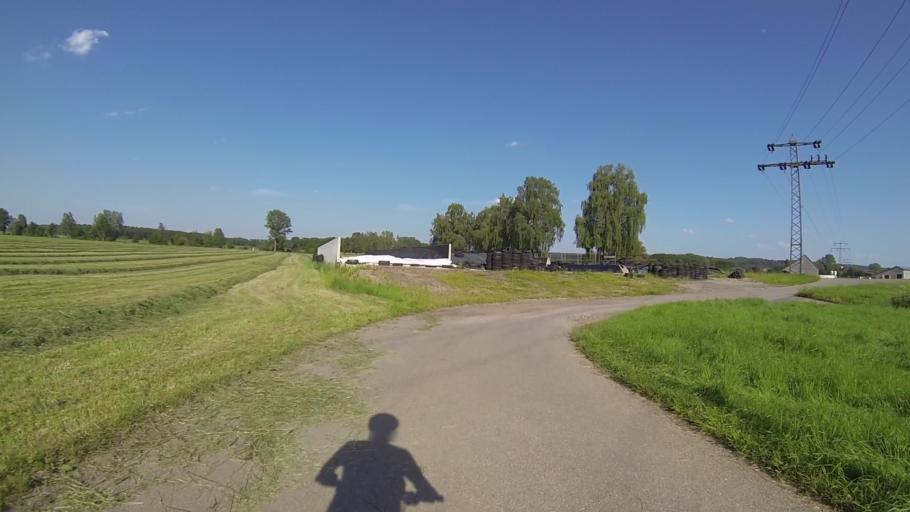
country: DE
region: Baden-Wuerttemberg
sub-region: Tuebingen Region
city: Warthausen
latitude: 48.1516
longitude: 9.7902
